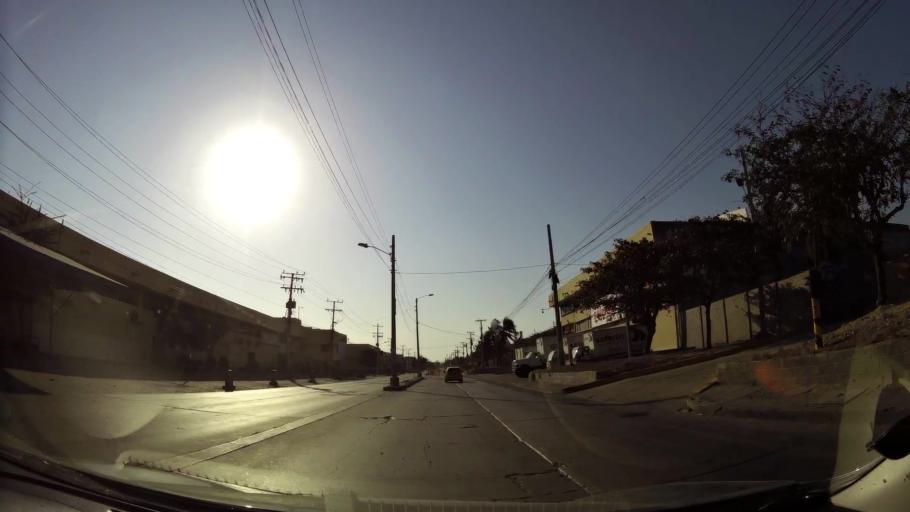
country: CO
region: Atlantico
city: Barranquilla
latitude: 11.0297
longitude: -74.8068
